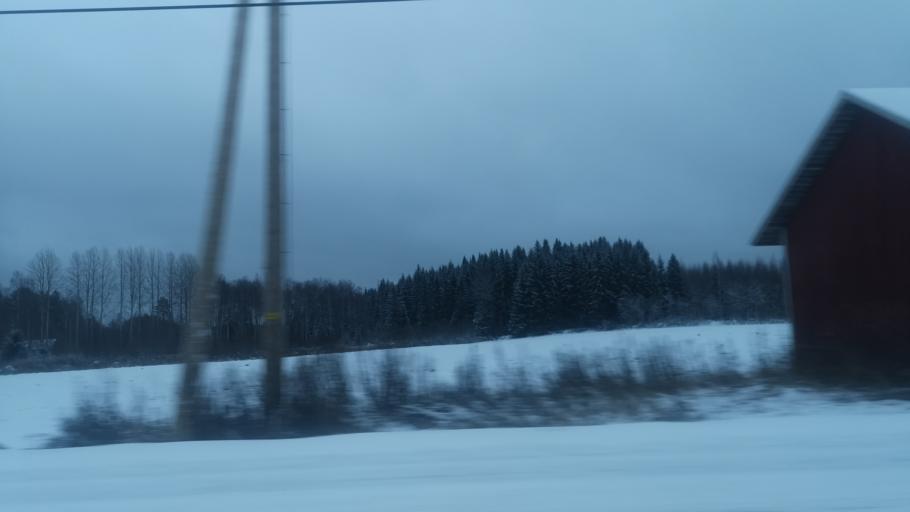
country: FI
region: Southern Savonia
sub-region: Savonlinna
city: Enonkoski
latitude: 62.0630
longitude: 28.7308
